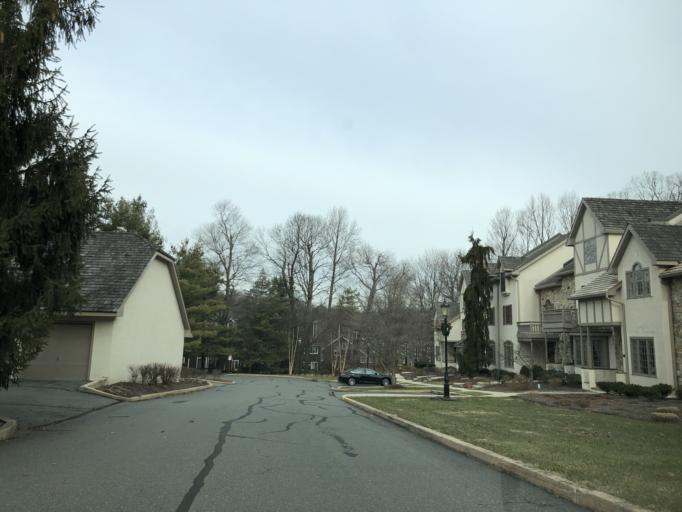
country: US
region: Pennsylvania
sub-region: Chester County
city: Exton
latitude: 40.0343
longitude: -75.6399
